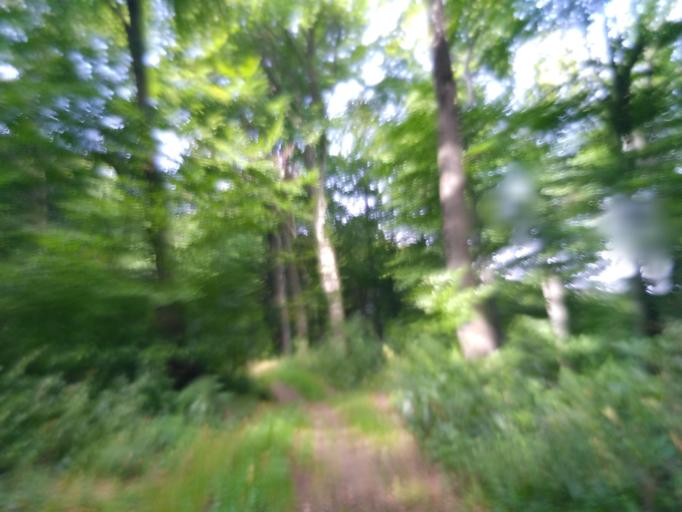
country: PL
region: Subcarpathian Voivodeship
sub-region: Powiat strzyzowski
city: Frysztak
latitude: 49.8896
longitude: 21.5580
